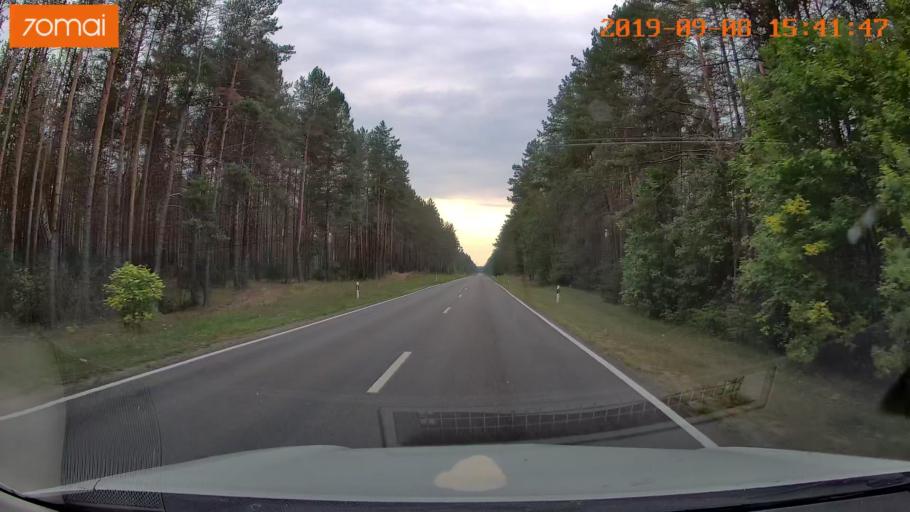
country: LT
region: Alytaus apskritis
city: Druskininkai
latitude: 53.9774
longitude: 24.0006
